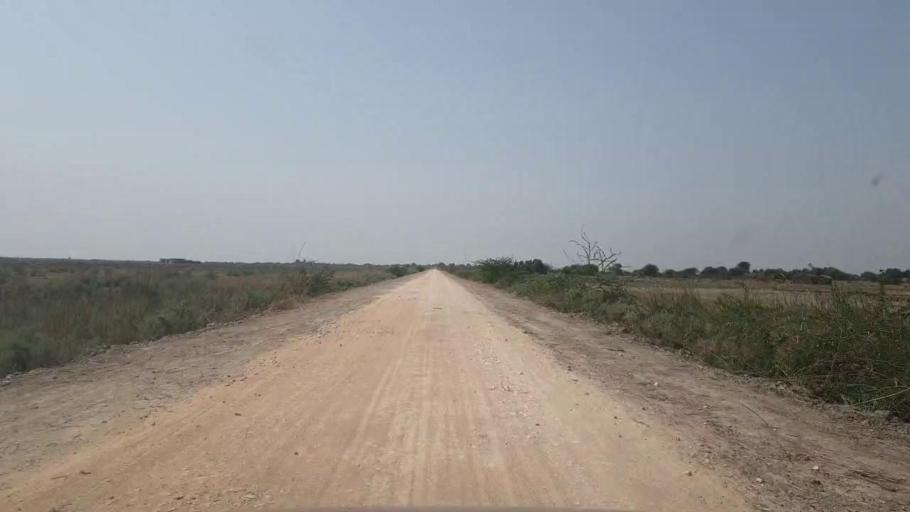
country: PK
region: Sindh
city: Jati
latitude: 24.3662
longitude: 68.5604
